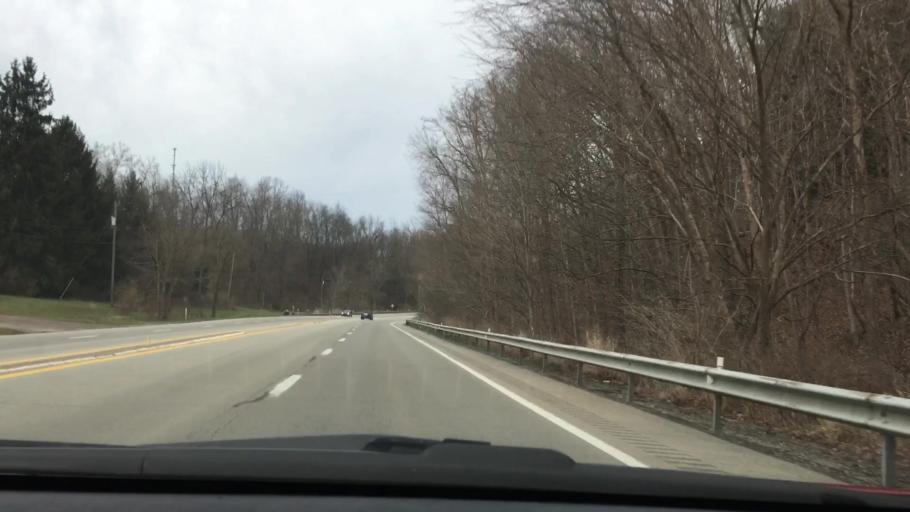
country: US
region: Pennsylvania
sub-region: Fayette County
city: Perryopolis
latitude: 40.0113
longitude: -79.7650
